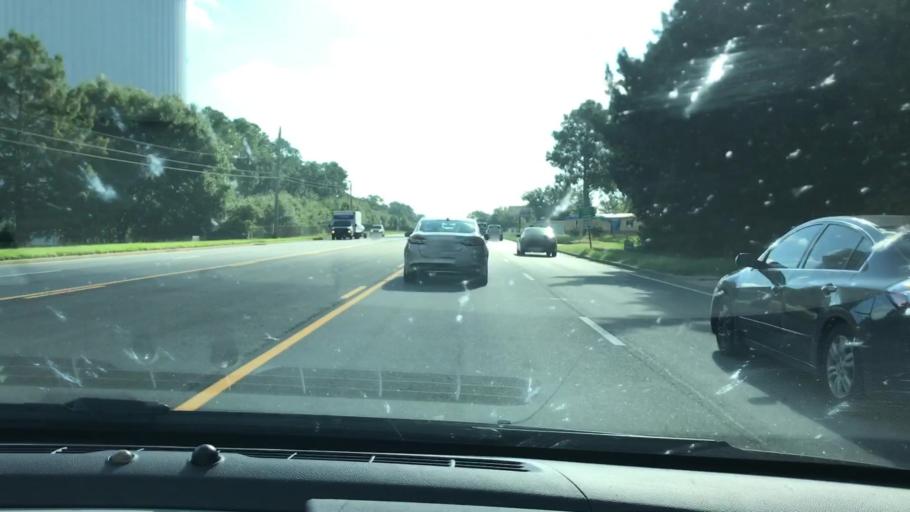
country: US
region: Georgia
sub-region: Dougherty County
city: Albany
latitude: 31.5799
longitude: -84.1017
